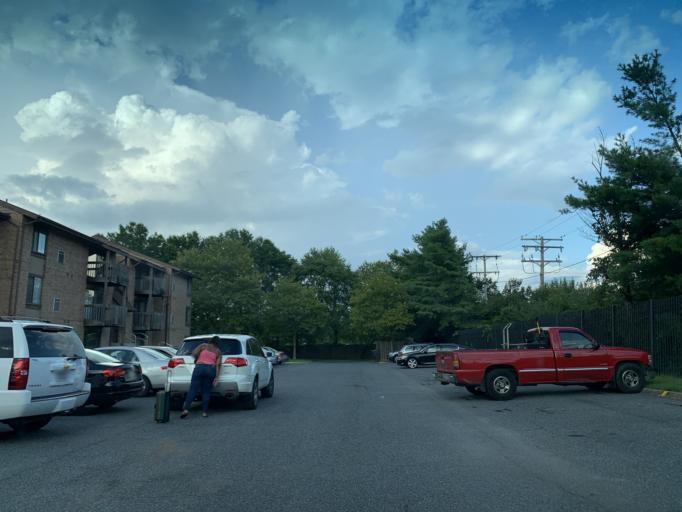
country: US
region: Maryland
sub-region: Baltimore County
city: Middle River
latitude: 39.2983
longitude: -76.4406
